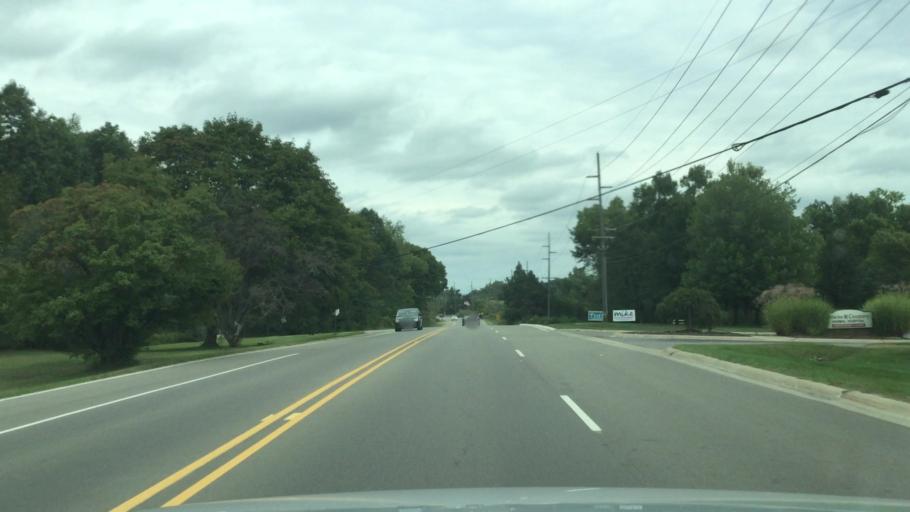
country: US
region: Michigan
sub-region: Livingston County
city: Brighton
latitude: 42.5399
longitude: -83.7530
